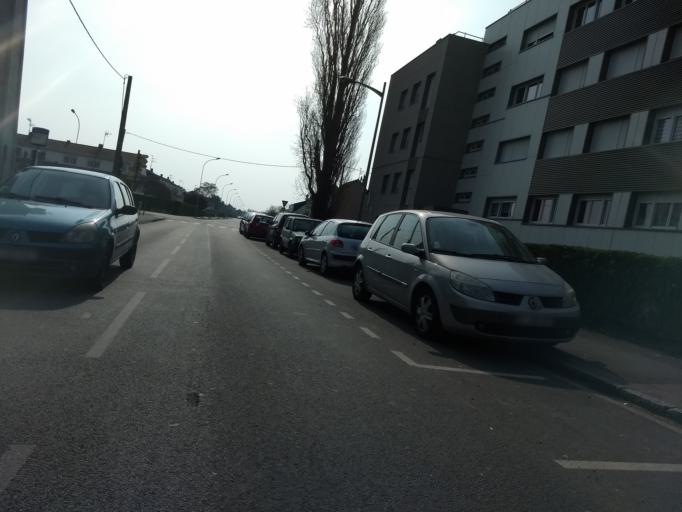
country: FR
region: Nord-Pas-de-Calais
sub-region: Departement du Pas-de-Calais
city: Beaurains
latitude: 50.2790
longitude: 2.7915
